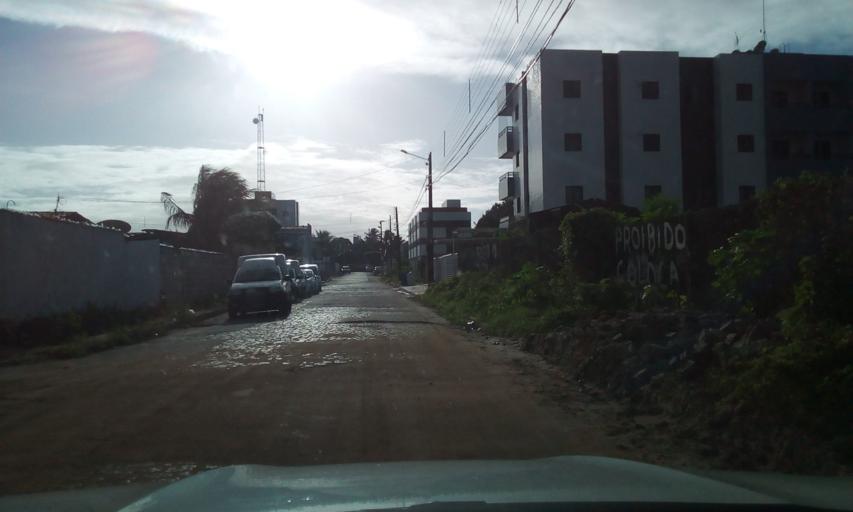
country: BR
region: Paraiba
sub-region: Joao Pessoa
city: Joao Pessoa
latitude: -7.1649
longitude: -34.8557
